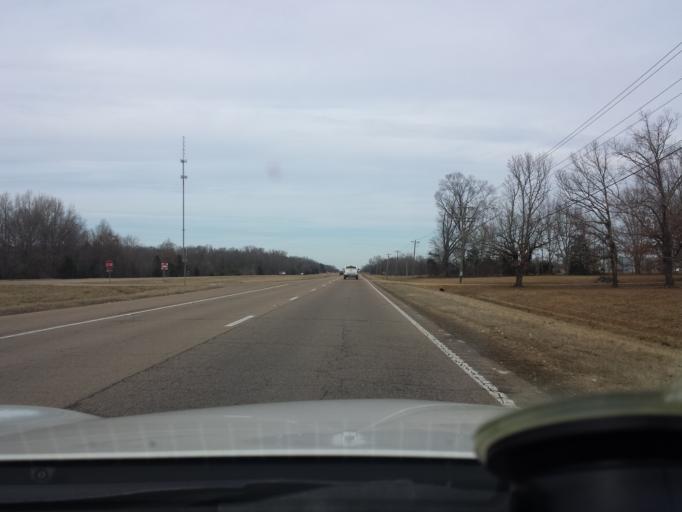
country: US
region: Mississippi
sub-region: Clay County
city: West Point
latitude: 33.6650
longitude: -88.6675
